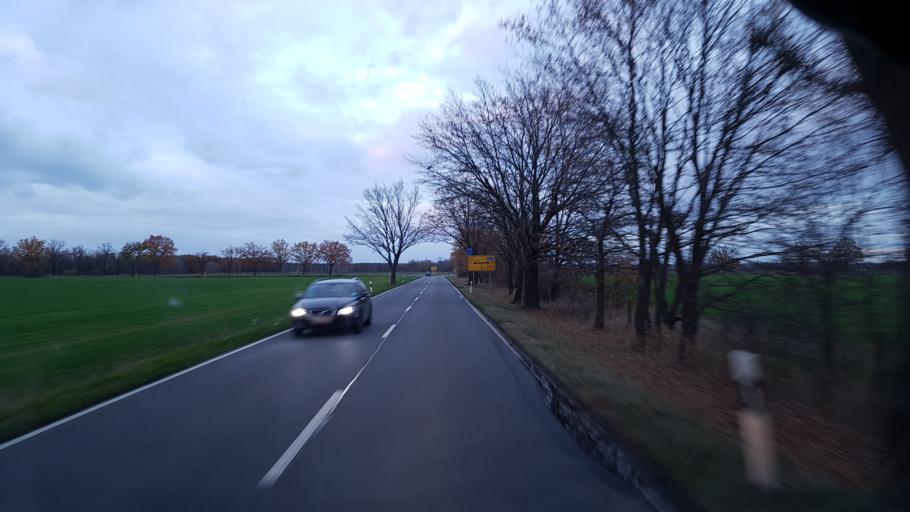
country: DE
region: Brandenburg
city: Schraden
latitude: 51.4638
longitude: 13.7124
